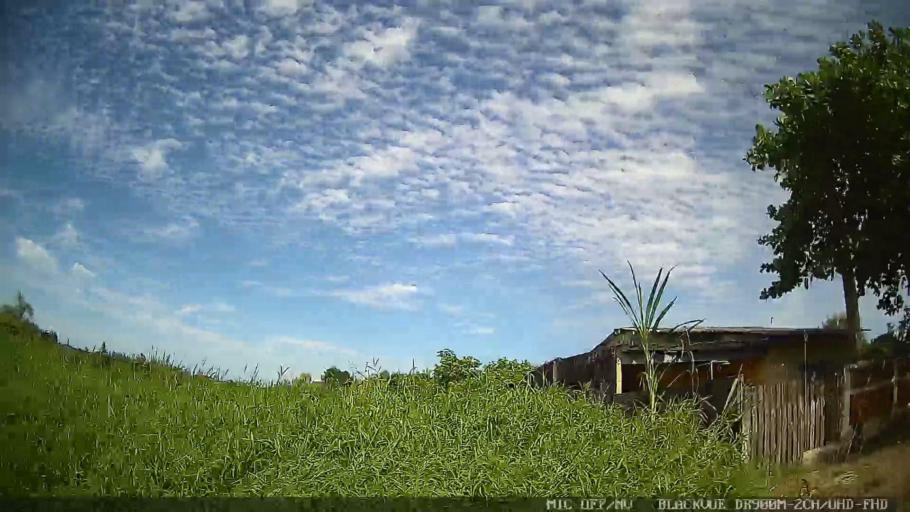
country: BR
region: Sao Paulo
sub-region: Iguape
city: Iguape
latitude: -24.7676
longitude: -47.5864
